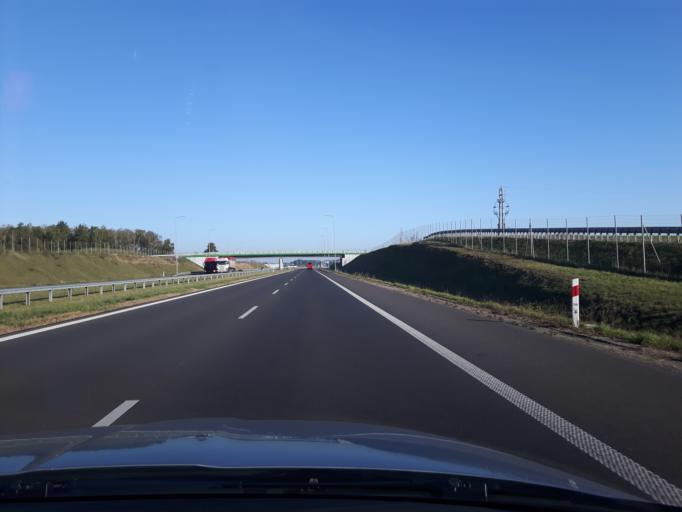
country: PL
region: Warmian-Masurian Voivodeship
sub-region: Powiat nidzicki
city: Nidzica
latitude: 53.2936
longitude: 20.4379
